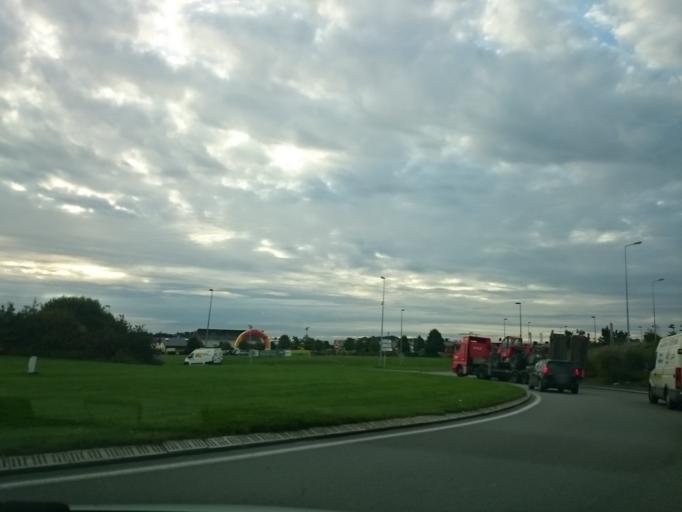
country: FR
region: Brittany
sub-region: Departement du Finistere
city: Gouesnou
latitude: 48.4187
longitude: -4.4399
